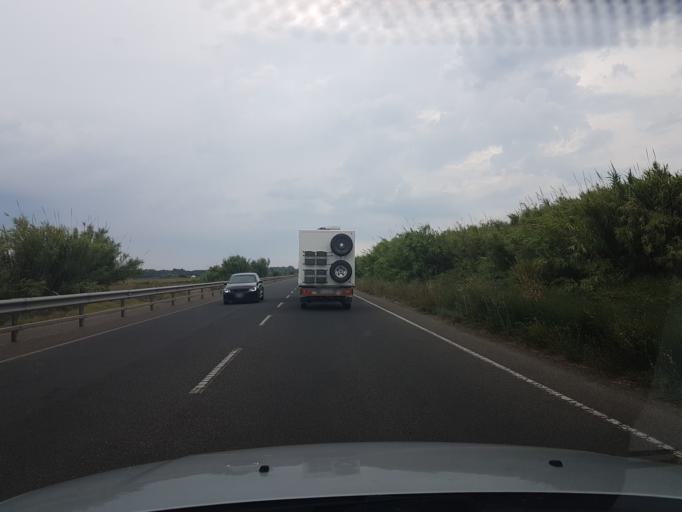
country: IT
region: Sardinia
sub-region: Provincia di Oristano
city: Cabras
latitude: 39.9135
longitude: 8.5391
